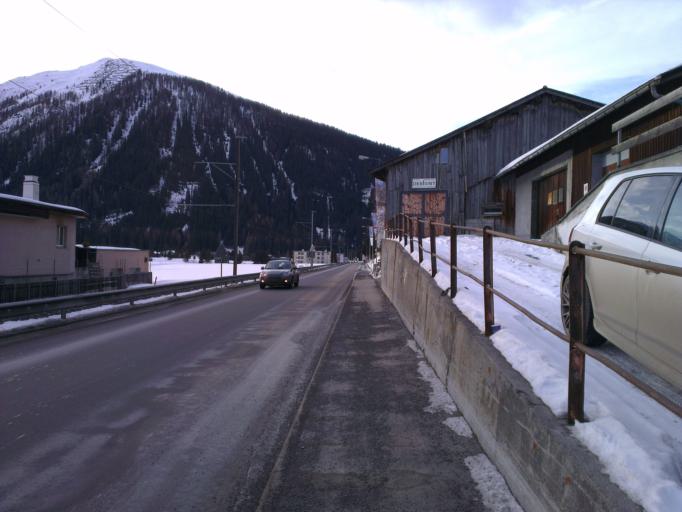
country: CH
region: Grisons
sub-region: Praettigau/Davos District
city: Davos
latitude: 46.8057
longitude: 9.8383
